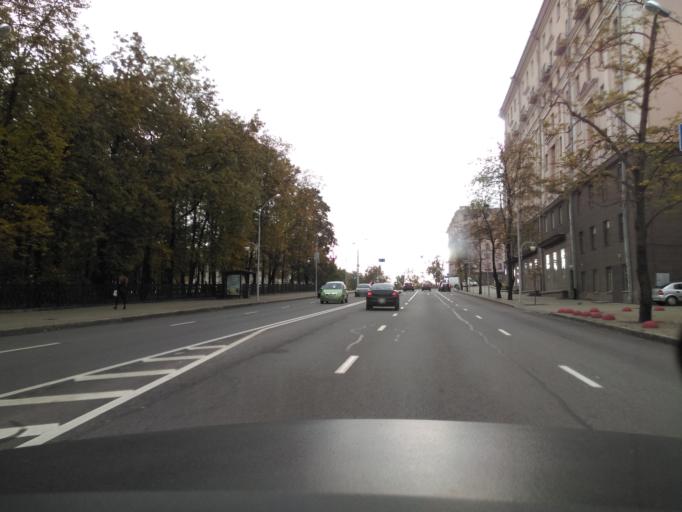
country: BY
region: Minsk
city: Minsk
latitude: 53.9052
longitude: 27.5650
